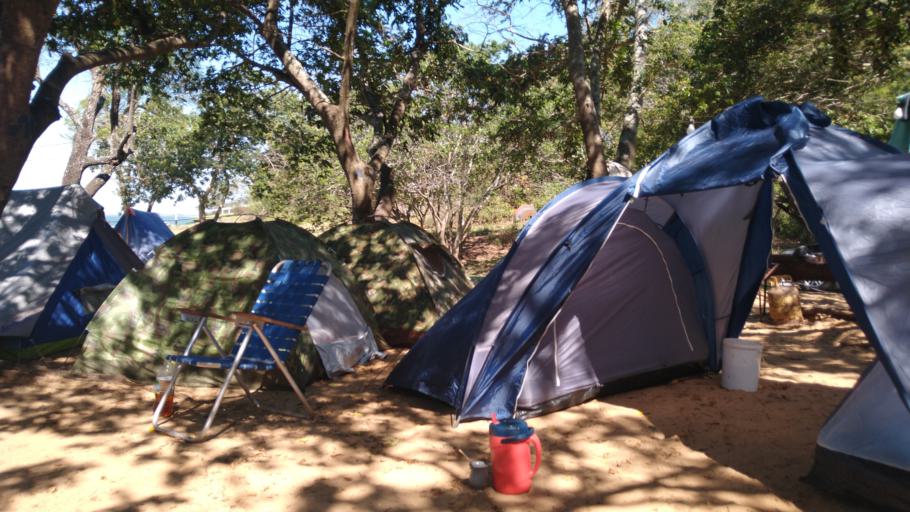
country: PY
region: Neembucu
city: Cerrito
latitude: -27.3691
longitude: -57.6564
